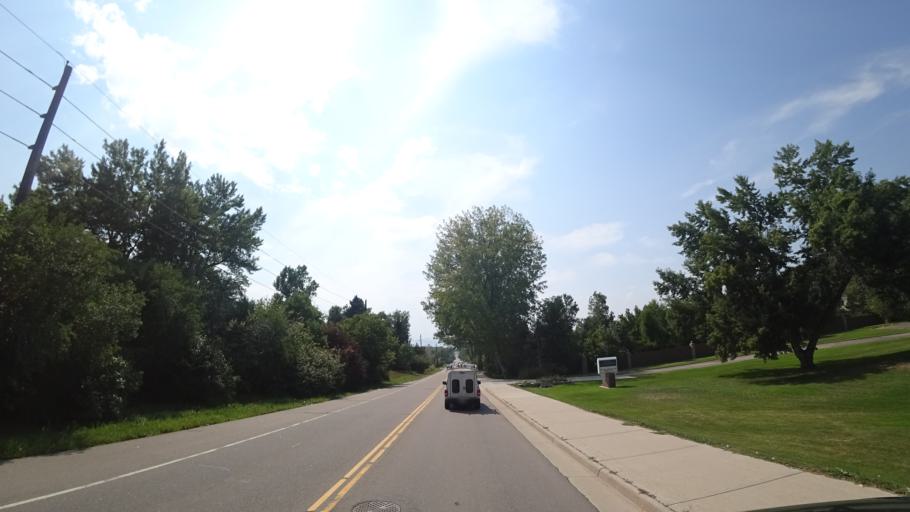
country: US
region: Colorado
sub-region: Arapahoe County
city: Greenwood Village
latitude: 39.6097
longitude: -104.9670
